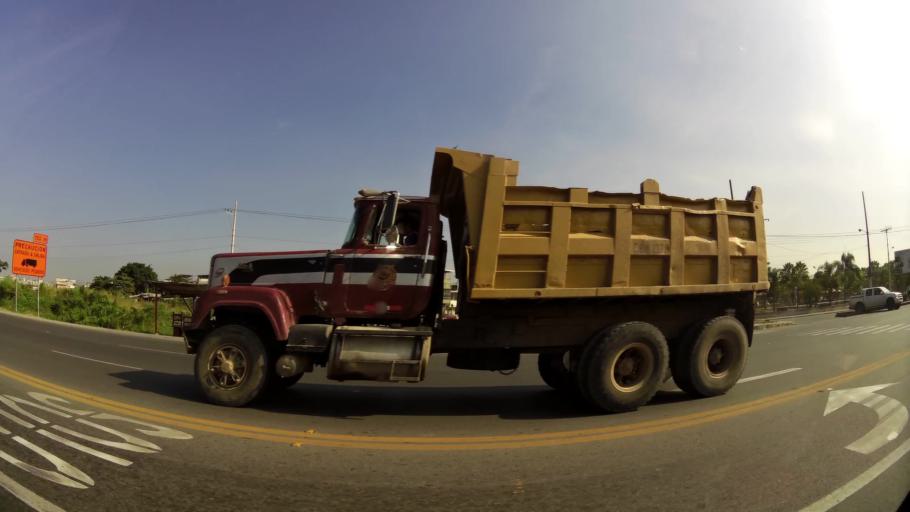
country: EC
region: Guayas
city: Eloy Alfaro
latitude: -2.1688
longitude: -79.7935
